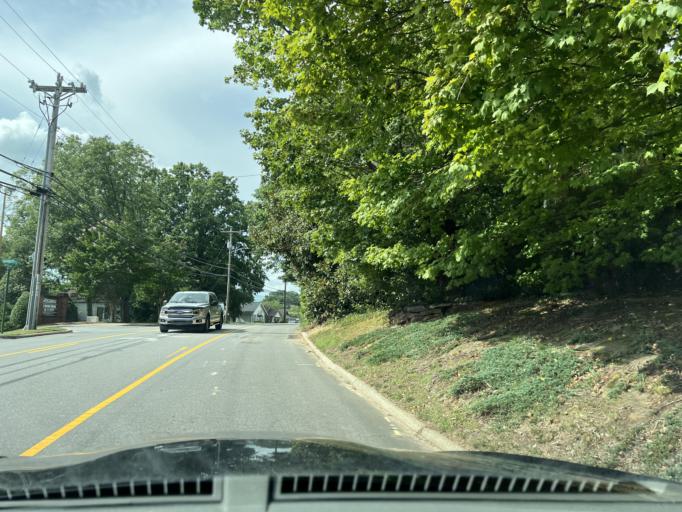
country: US
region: North Carolina
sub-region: Iredell County
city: Statesville
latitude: 35.7961
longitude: -80.8765
